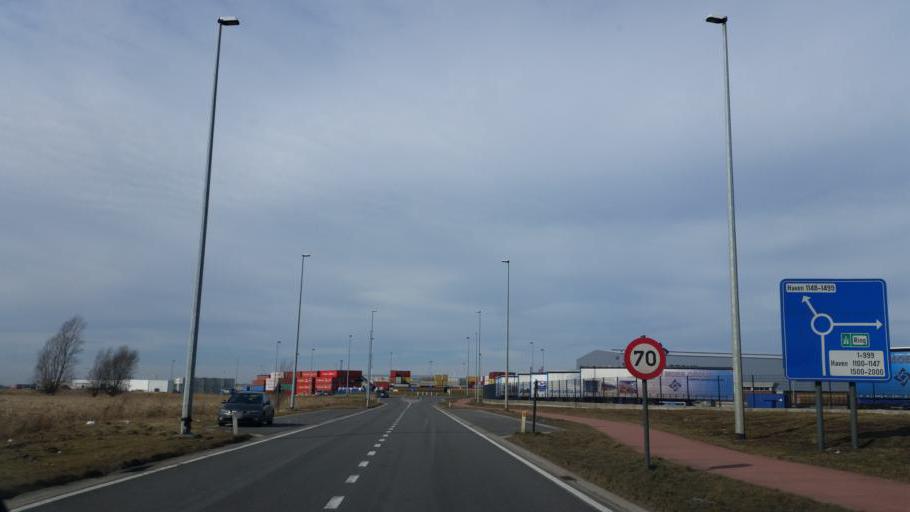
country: BE
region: Flanders
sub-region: Provincie Oost-Vlaanderen
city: Beveren
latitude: 51.2483
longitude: 4.2518
